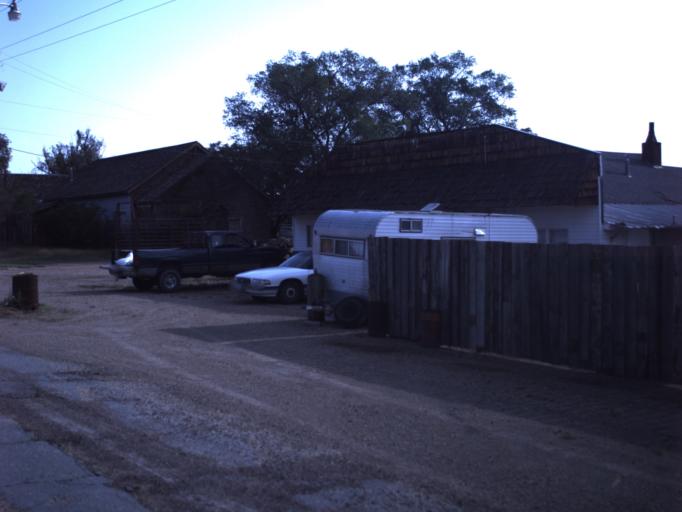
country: US
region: Utah
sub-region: Duchesne County
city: Duchesne
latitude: 40.3489
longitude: -110.2752
